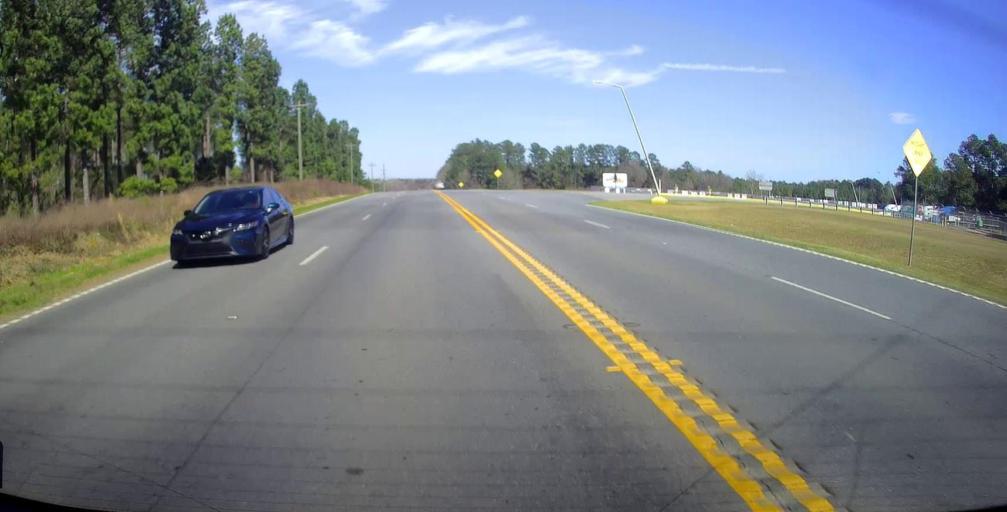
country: US
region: Georgia
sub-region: Houston County
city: Perry
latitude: 32.4450
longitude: -83.6307
